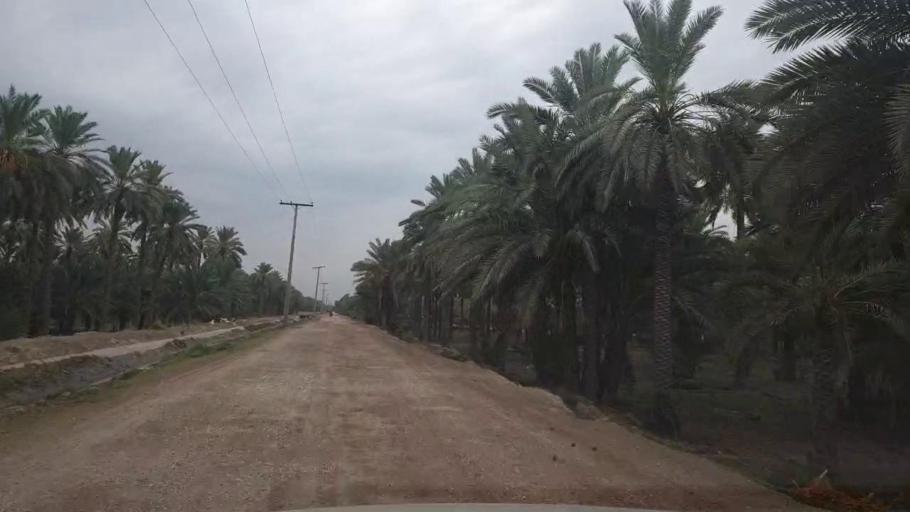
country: PK
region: Sindh
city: Khairpur
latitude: 27.6127
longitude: 68.8177
